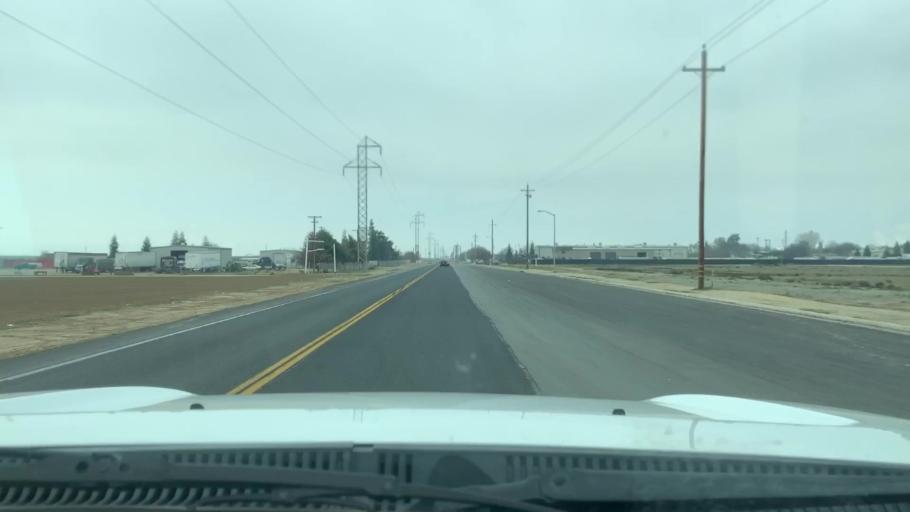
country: US
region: California
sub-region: Kern County
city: Shafter
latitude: 35.4417
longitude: -119.2439
